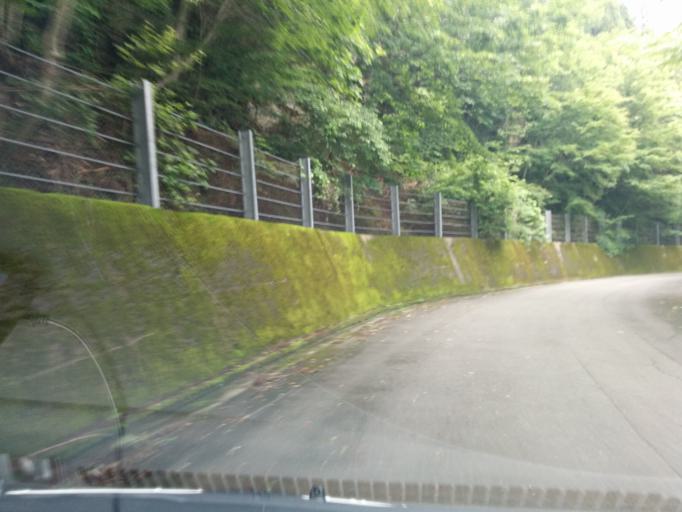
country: JP
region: Kyoto
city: Miyazu
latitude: 35.4503
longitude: 135.1125
